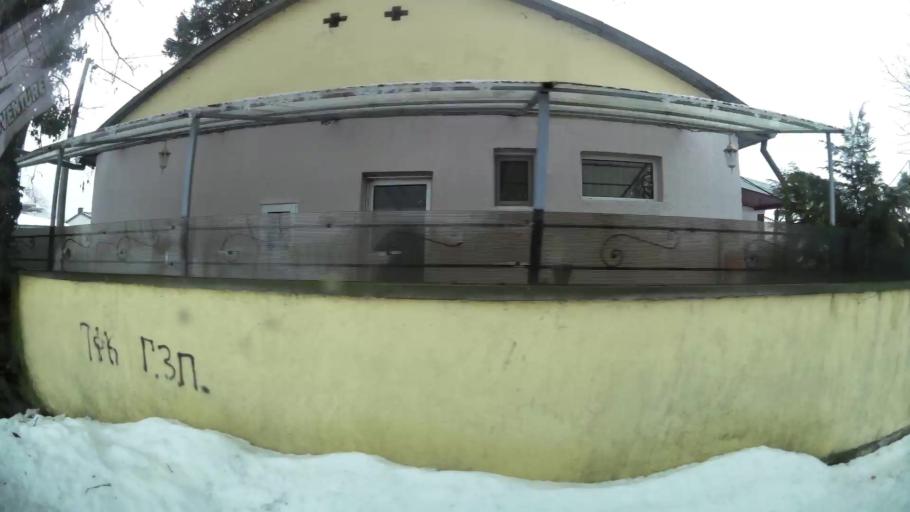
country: RS
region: Central Serbia
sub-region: Belgrade
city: Zemun
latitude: 44.8685
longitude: 20.3206
